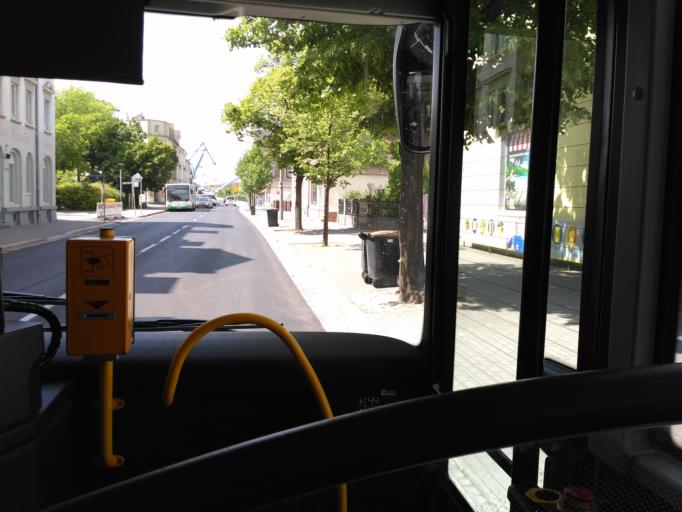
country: DE
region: Saxony
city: Riesa
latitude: 51.3173
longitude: 13.2837
